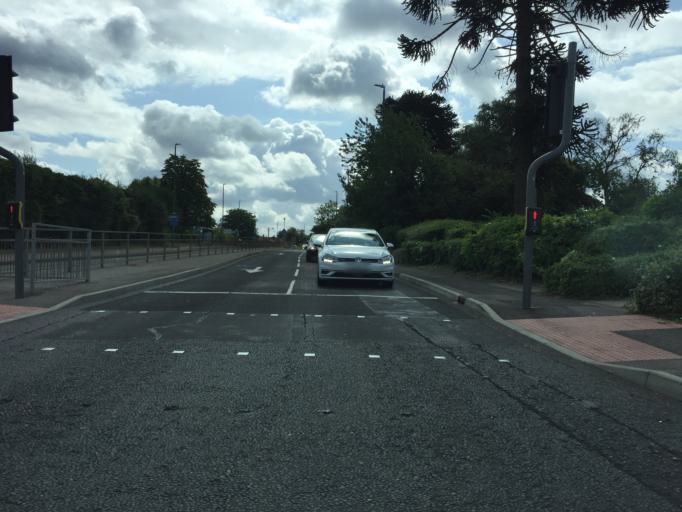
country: GB
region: England
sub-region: Kent
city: Aylesford
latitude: 51.2881
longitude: 0.4903
